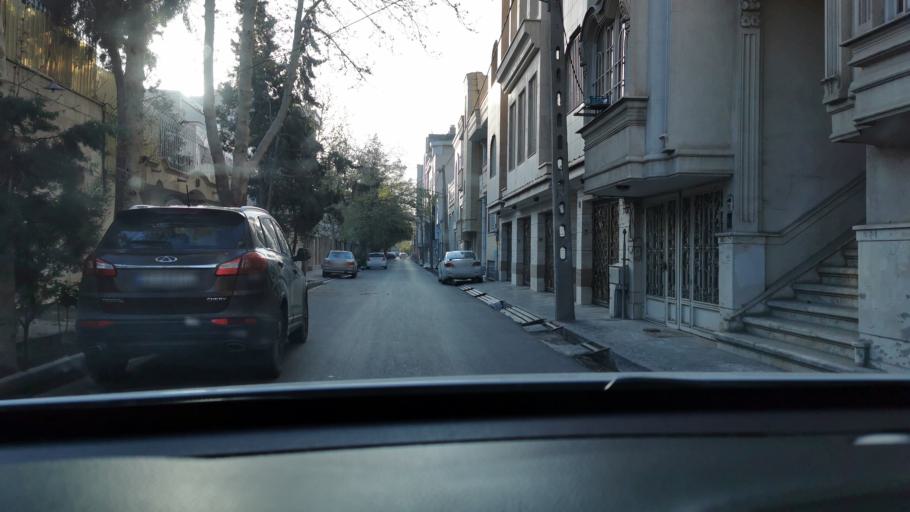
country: IR
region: Razavi Khorasan
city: Mashhad
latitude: 36.2956
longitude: 59.5792
